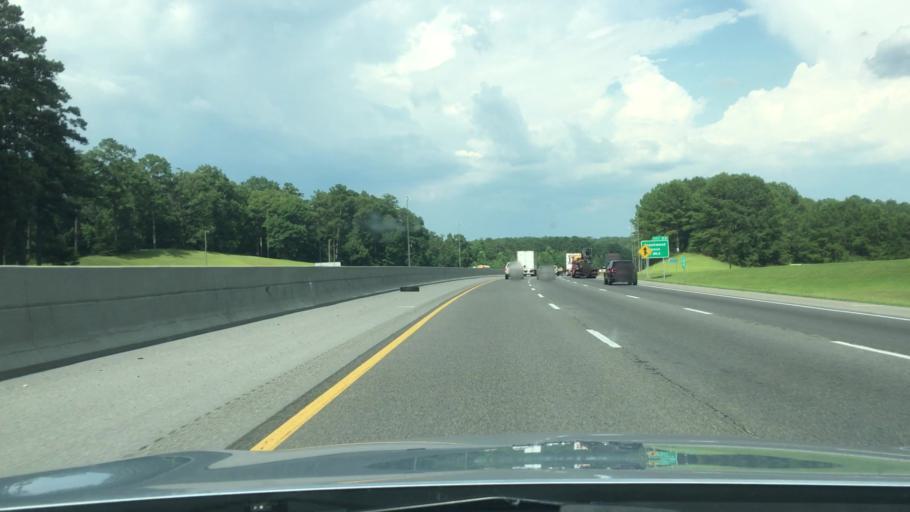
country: US
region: Alabama
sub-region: Tuscaloosa County
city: Coaling
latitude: 33.1901
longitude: -87.3230
